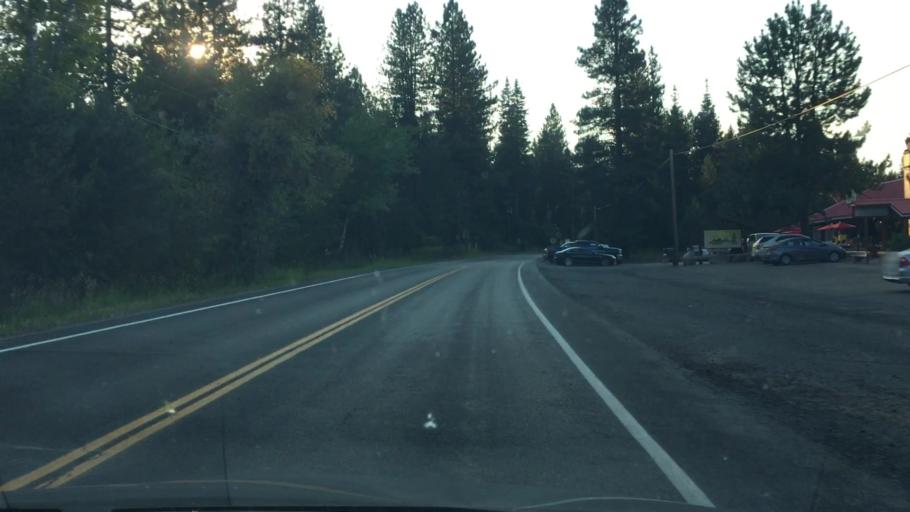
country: US
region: Idaho
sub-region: Valley County
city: McCall
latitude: 44.9146
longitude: -116.1302
